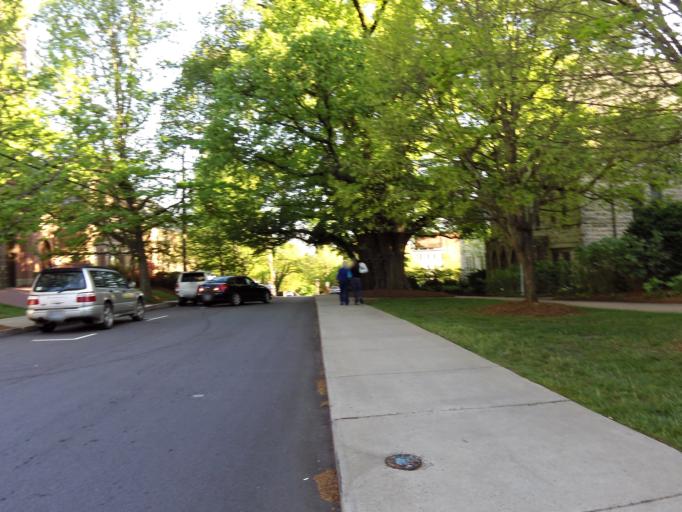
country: US
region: North Carolina
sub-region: Buncombe County
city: Asheville
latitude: 35.5938
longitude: -82.5534
